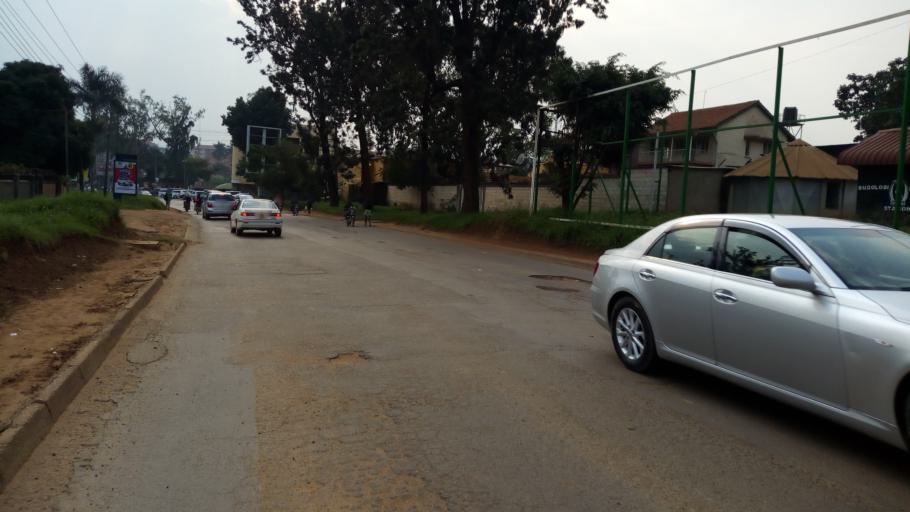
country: UG
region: Central Region
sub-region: Kampala District
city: Kampala
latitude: 0.3201
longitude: 32.6197
